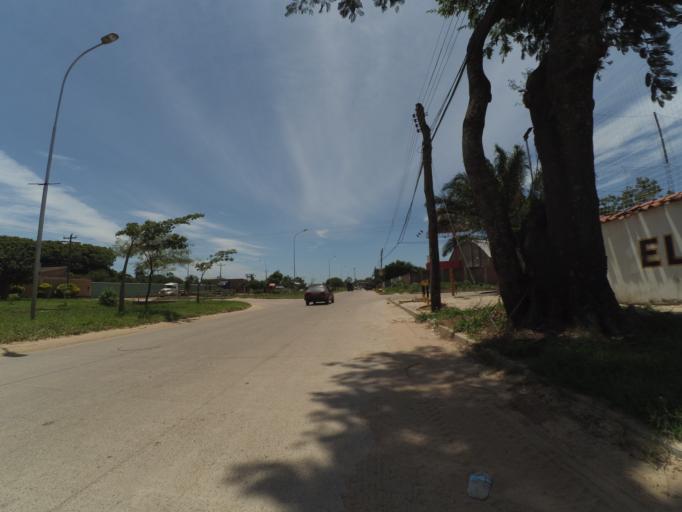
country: BO
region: Santa Cruz
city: Santa Cruz de la Sierra
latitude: -17.8111
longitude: -63.2220
